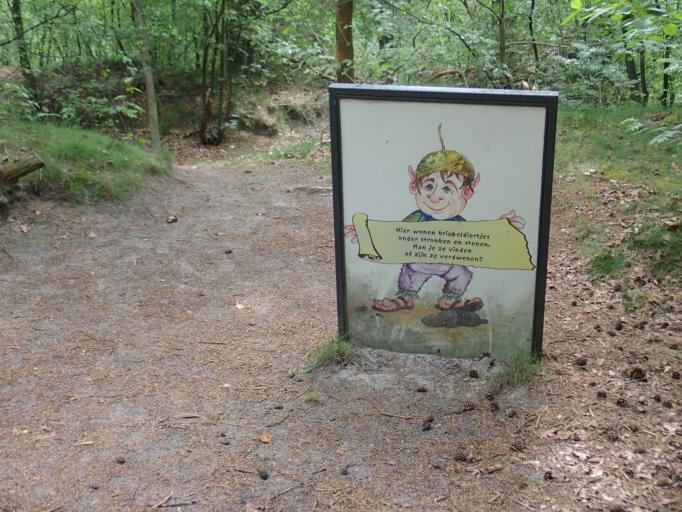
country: BE
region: Flanders
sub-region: Provincie Antwerpen
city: Oud-Turnhout
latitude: 51.3260
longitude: 5.0058
